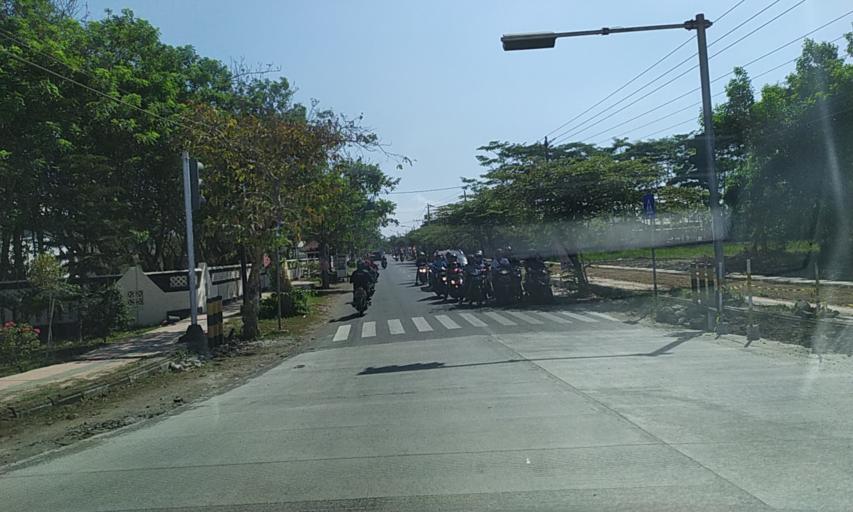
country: ID
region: Central Java
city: Karangbadar Kidul
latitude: -7.7174
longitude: 109.0206
